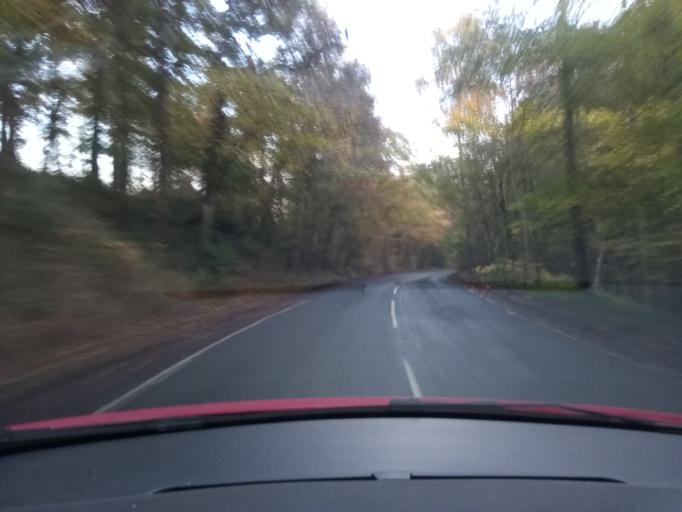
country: GB
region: England
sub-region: Northumberland
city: Bardon Mill
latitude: 54.9524
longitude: -2.2660
